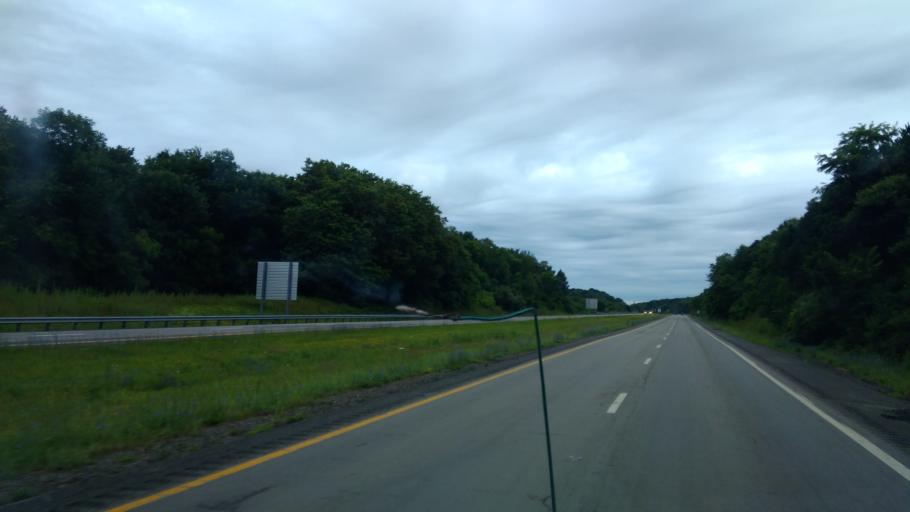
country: US
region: Ohio
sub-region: Columbiana County
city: Lisbon
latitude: 40.7733
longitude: -80.7328
